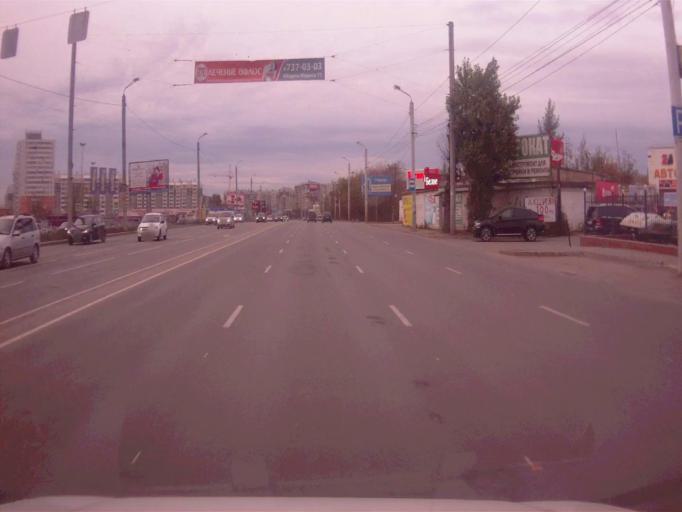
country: RU
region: Chelyabinsk
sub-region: Gorod Chelyabinsk
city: Chelyabinsk
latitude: 55.1758
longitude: 61.3789
